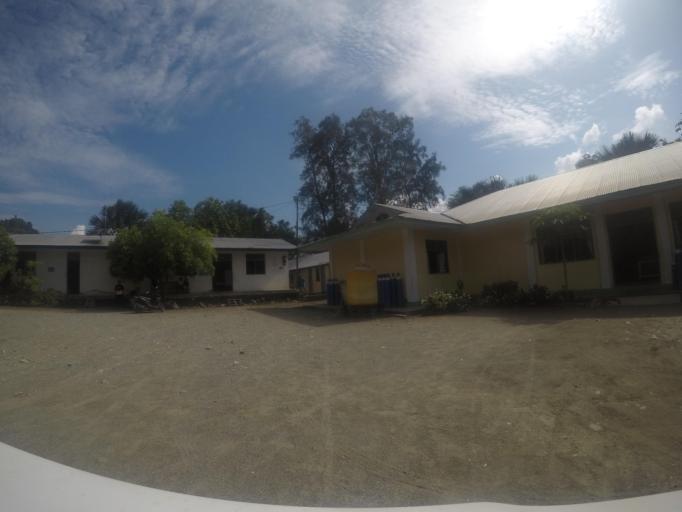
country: TL
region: Viqueque
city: Viqueque
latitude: -8.8525
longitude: 126.3581
